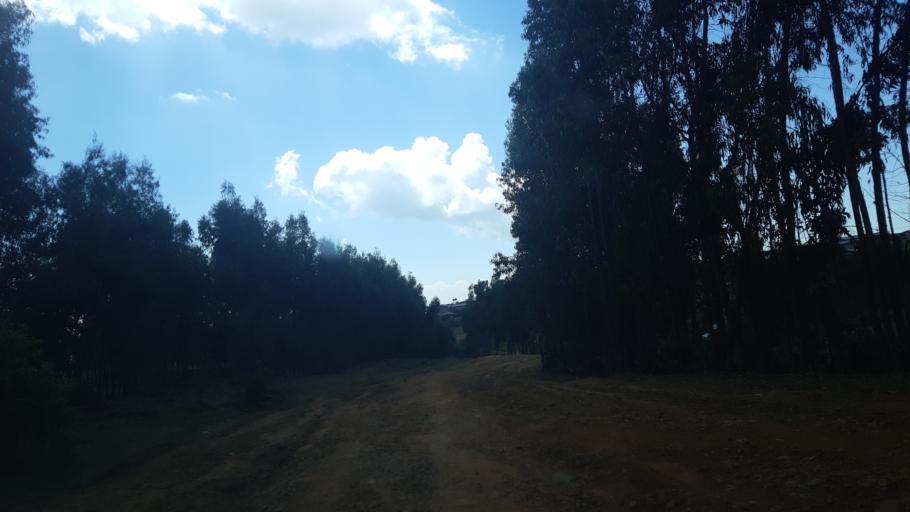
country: ET
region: Amhara
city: Dabat
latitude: 13.3582
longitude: 37.3848
